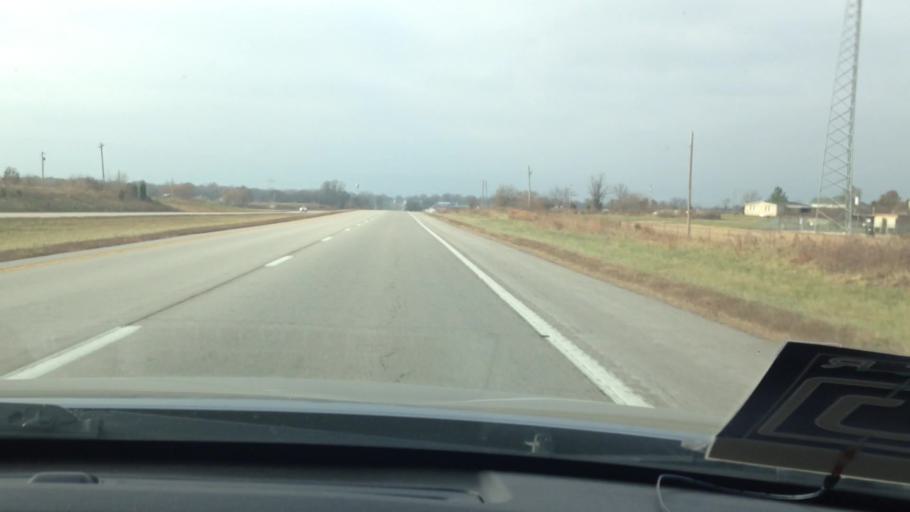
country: US
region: Missouri
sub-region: Cass County
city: Garden City
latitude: 38.5500
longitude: -94.1735
